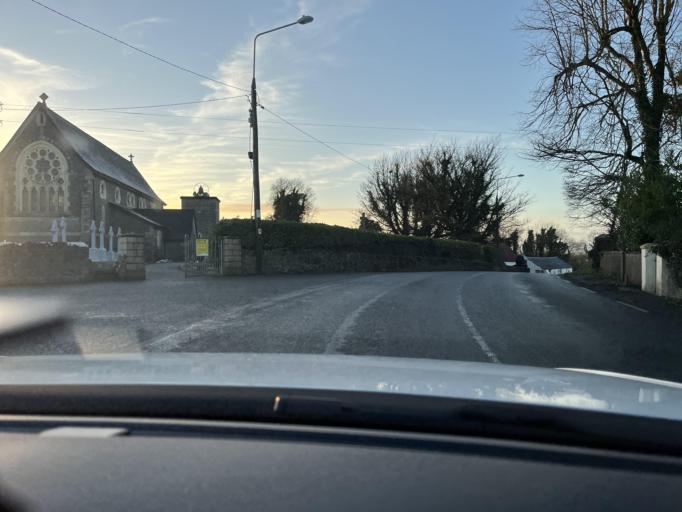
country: IE
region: Ulster
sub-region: An Cabhan
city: Ballyconnell
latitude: 54.0866
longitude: -7.6449
